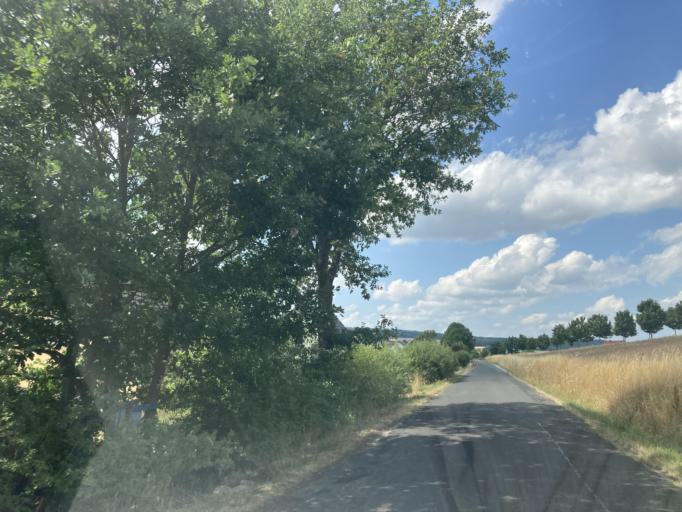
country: DE
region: Hesse
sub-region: Regierungsbezirk Kassel
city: Hosenfeld
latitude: 50.5421
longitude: 9.5199
